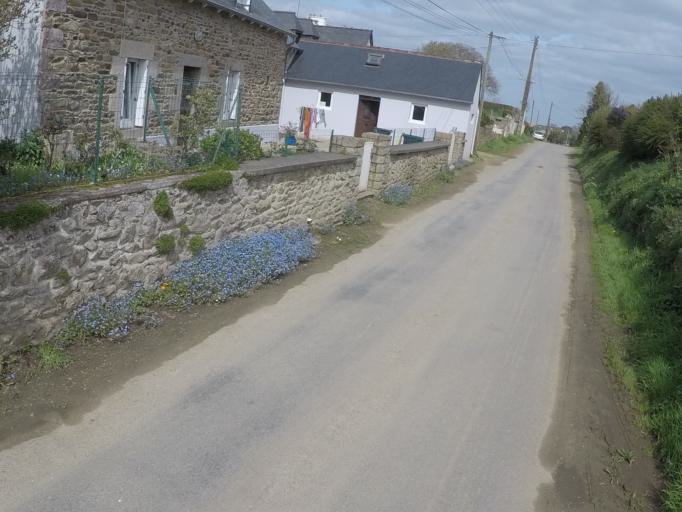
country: FR
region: Brittany
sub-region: Departement des Cotes-d'Armor
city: Plouha
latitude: 48.7107
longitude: -2.9423
